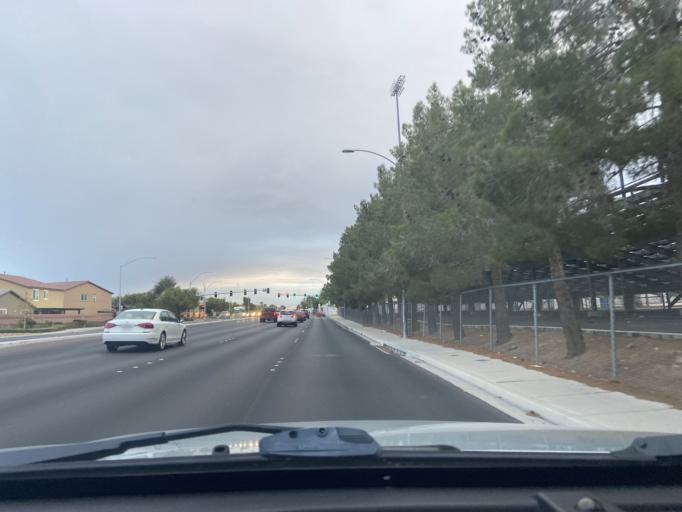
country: US
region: Nevada
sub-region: Clark County
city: North Las Vegas
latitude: 36.2333
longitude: -115.1803
